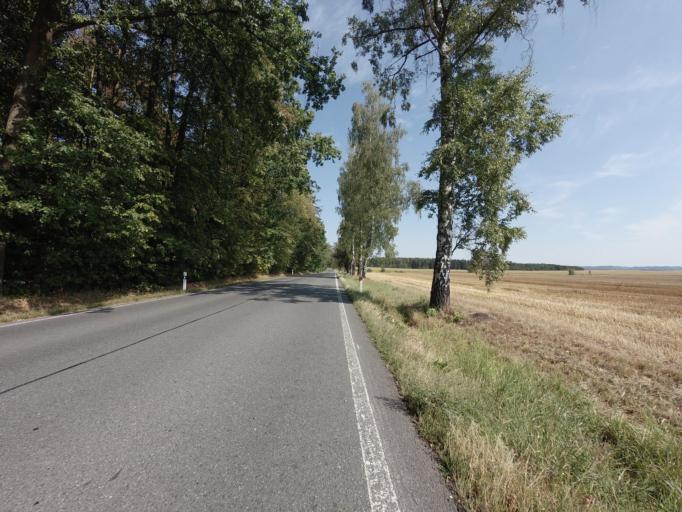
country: CZ
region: Jihocesky
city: Milevsko
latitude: 49.4178
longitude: 14.3582
